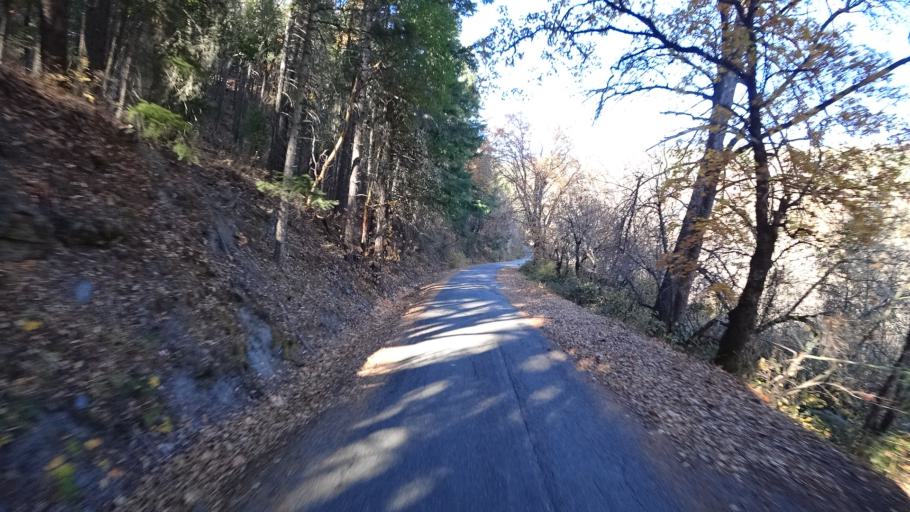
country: US
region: California
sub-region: Siskiyou County
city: Yreka
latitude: 41.8448
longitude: -122.9011
